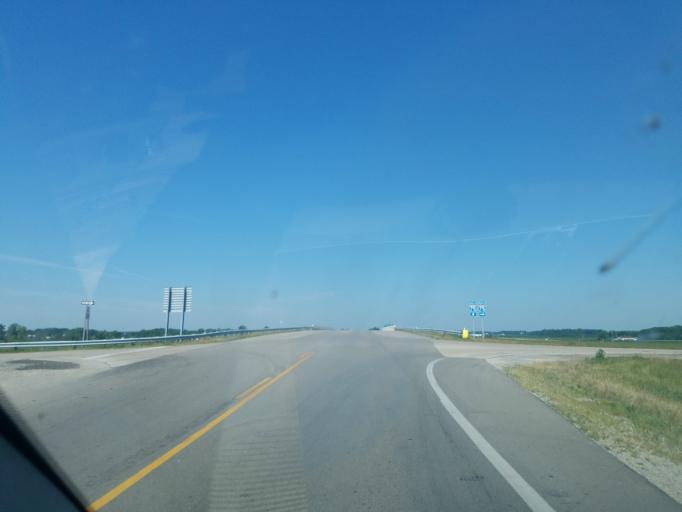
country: US
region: Ohio
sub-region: Shelby County
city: Botkins
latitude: 40.4388
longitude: -84.1678
